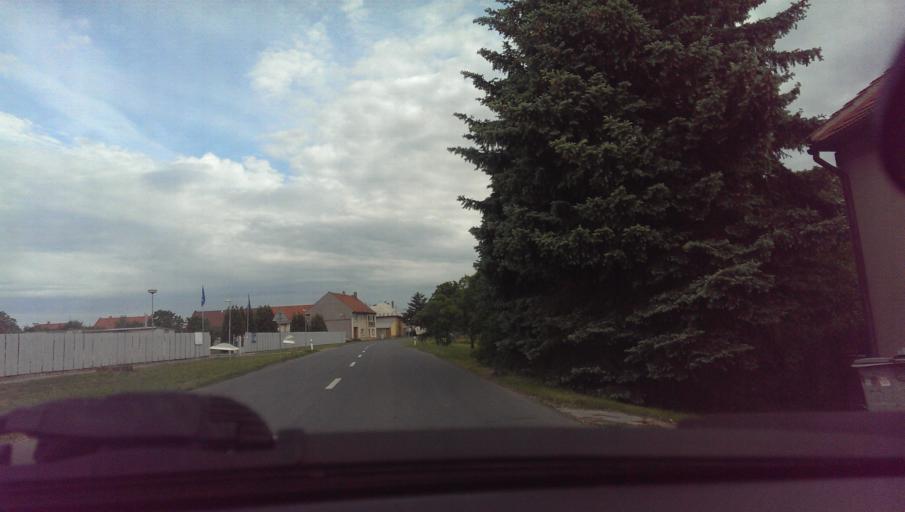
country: CZ
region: Zlin
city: Kvasice
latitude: 49.2552
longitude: 17.4485
